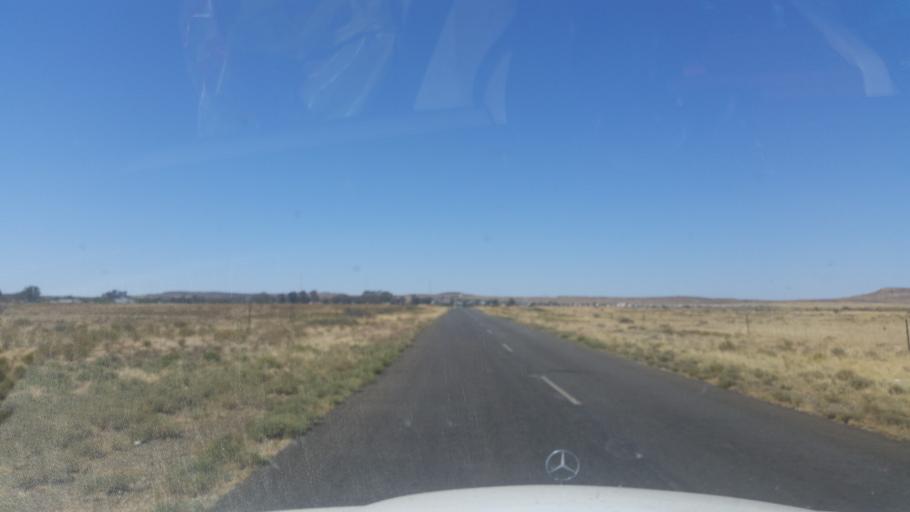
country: ZA
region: Eastern Cape
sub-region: Joe Gqabi District Municipality
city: Burgersdorp
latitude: -30.7653
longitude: 25.7872
